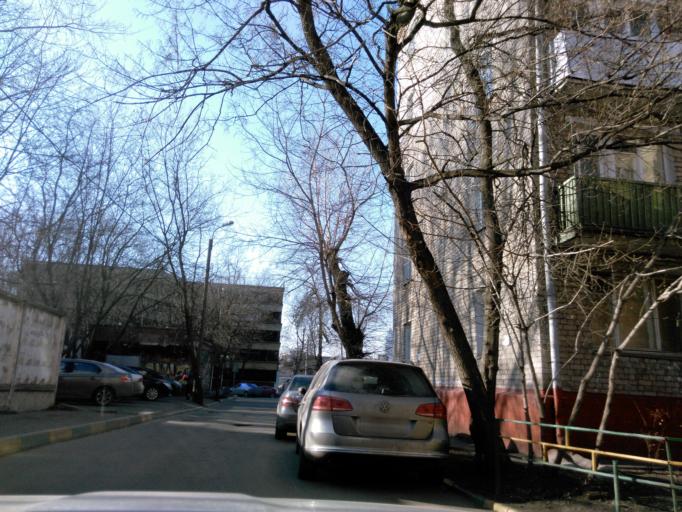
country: RU
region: Moskovskaya
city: Koptevo
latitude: 55.8167
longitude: 37.5258
